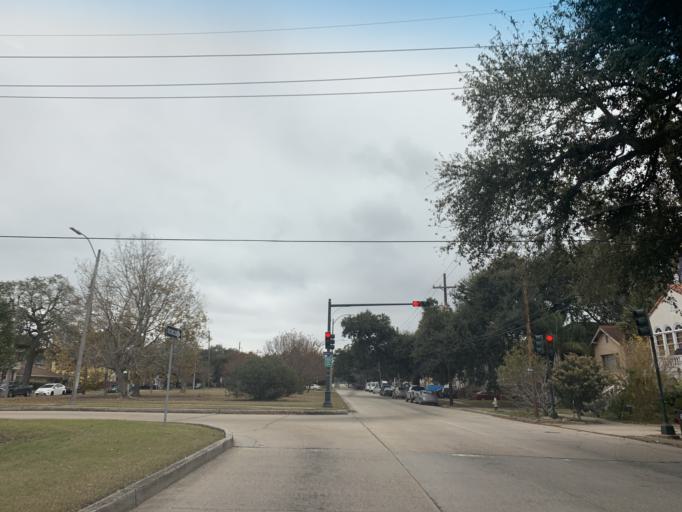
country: US
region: Louisiana
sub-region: Jefferson Parish
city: Metairie
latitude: 29.9901
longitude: -90.1099
